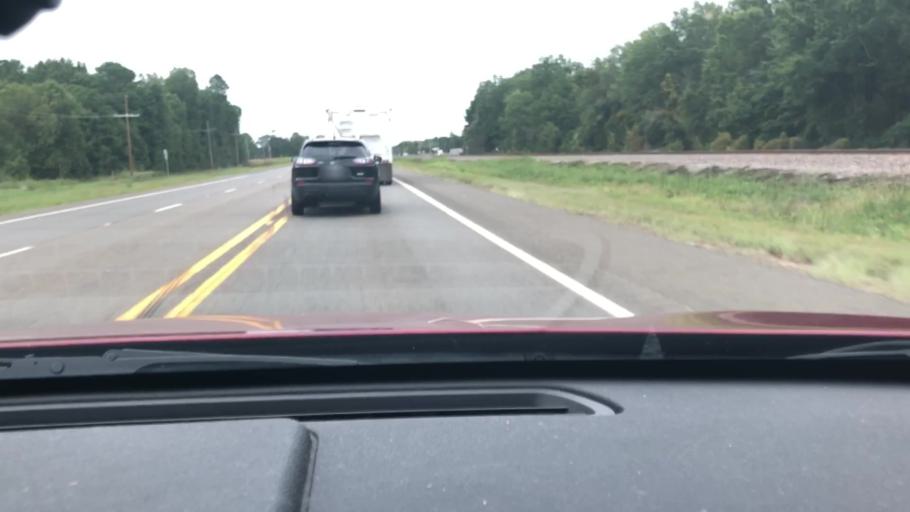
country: US
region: Arkansas
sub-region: Lafayette County
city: Lewisville
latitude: 33.3570
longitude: -93.5944
